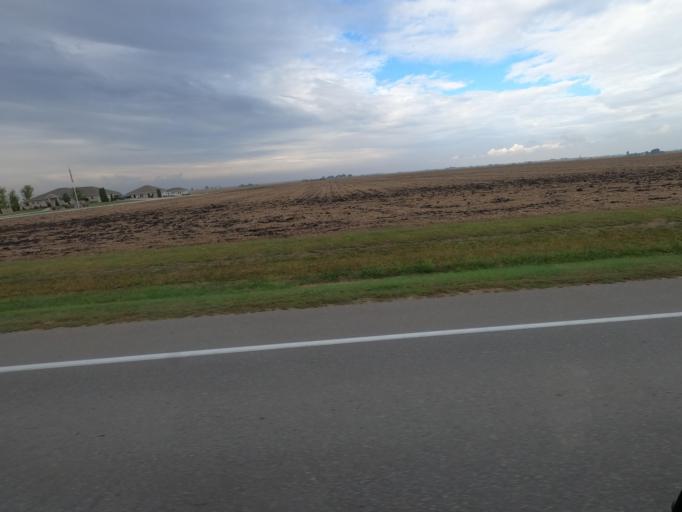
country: US
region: Iowa
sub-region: Henry County
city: Mount Pleasant
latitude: 40.7847
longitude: -91.6118
